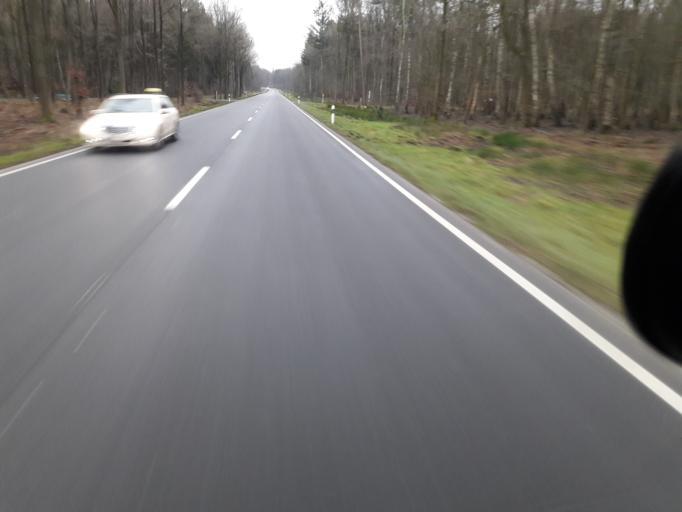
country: DE
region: Lower Saxony
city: Bad Bentheim
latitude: 52.3275
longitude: 7.1549
